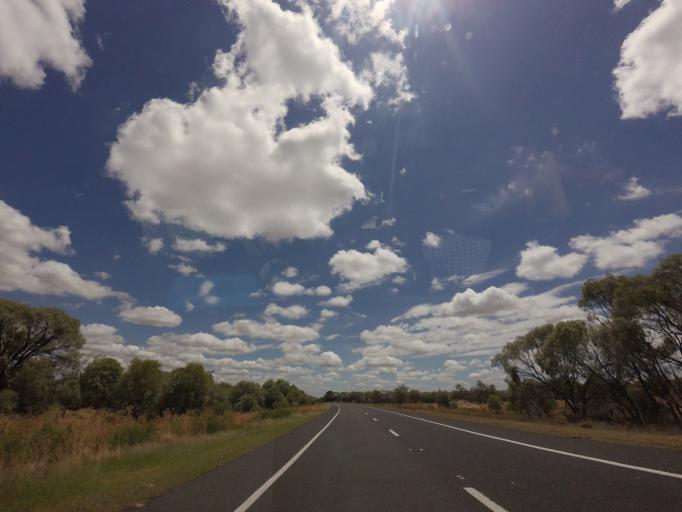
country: AU
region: New South Wales
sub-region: Moree Plains
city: Boggabilla
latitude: -28.9924
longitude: 150.0754
